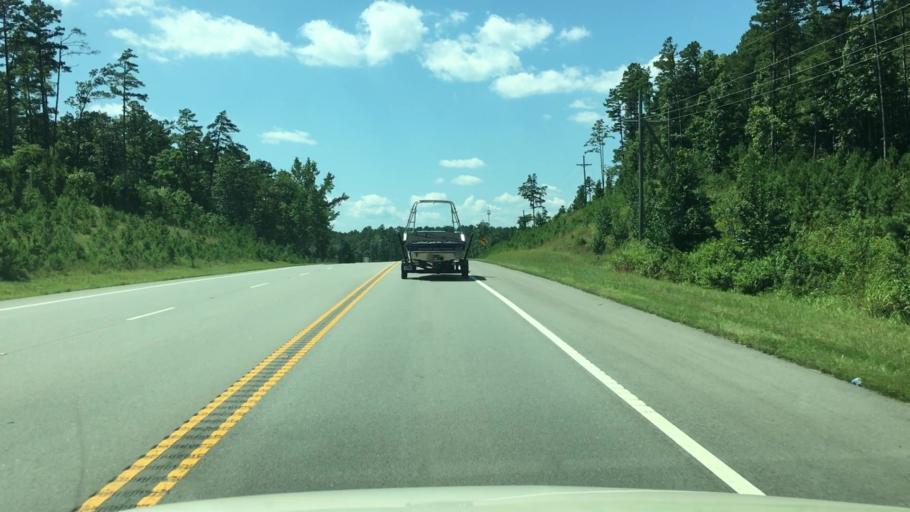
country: US
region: Arkansas
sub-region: Garland County
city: Rockwell
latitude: 34.5195
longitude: -93.3150
